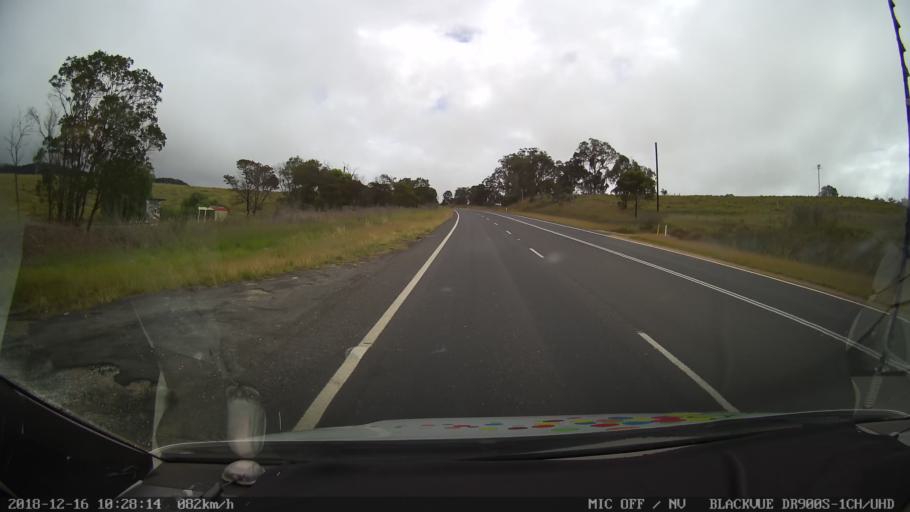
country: AU
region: New South Wales
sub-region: Tenterfield Municipality
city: Carrolls Creek
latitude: -29.1238
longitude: 151.9973
